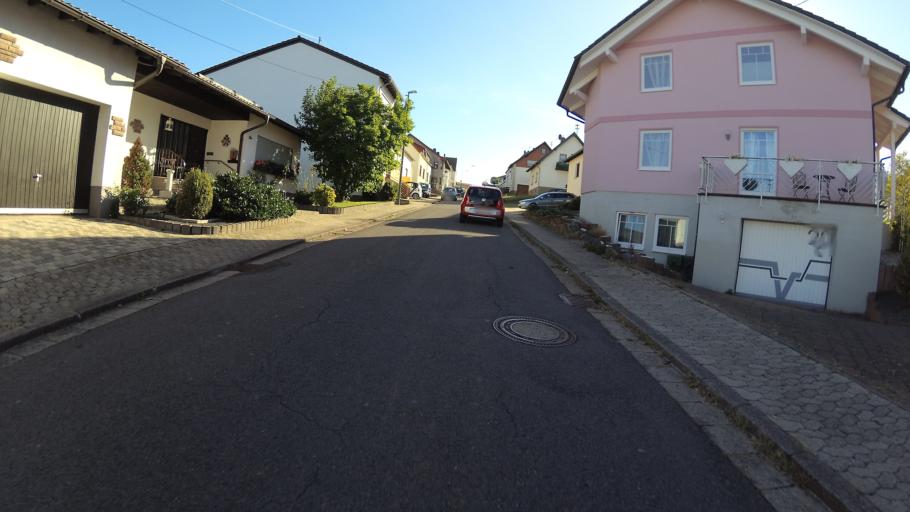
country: DE
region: Saarland
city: Eppelborn
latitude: 49.4027
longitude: 6.9555
